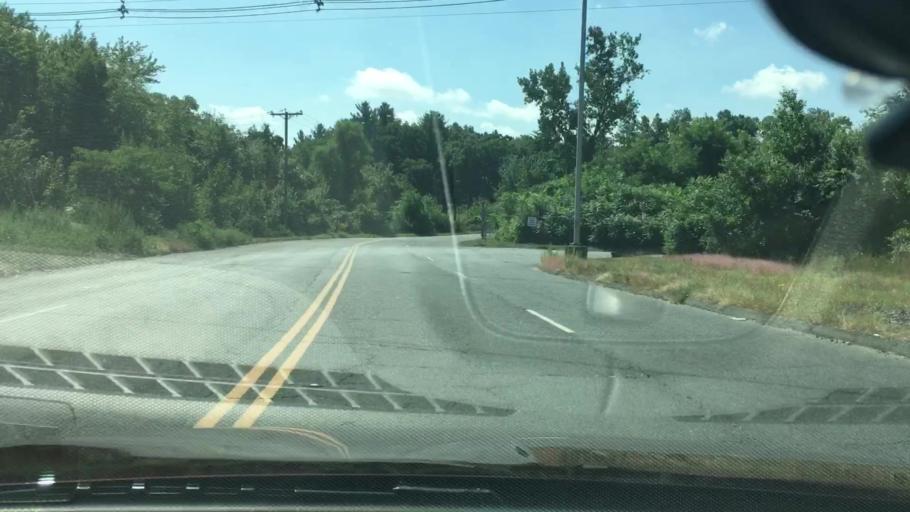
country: US
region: Connecticut
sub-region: Hartford County
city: Bristol
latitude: 41.6486
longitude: -72.9096
